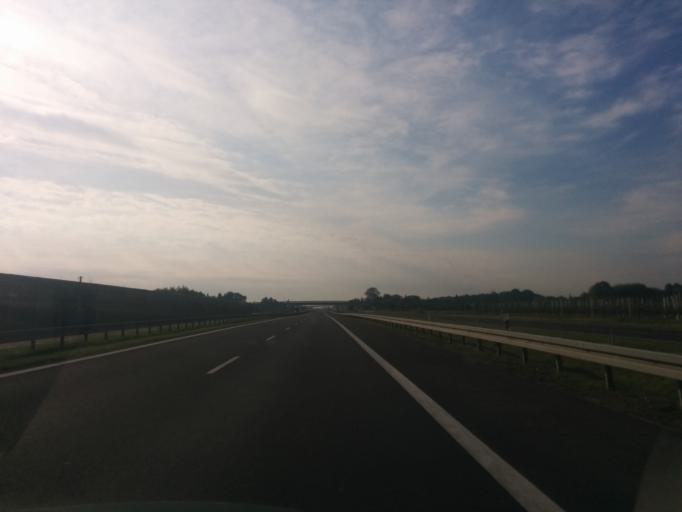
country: PL
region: Masovian Voivodeship
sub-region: Powiat grojecki
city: Jasieniec
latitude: 51.8018
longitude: 20.8885
